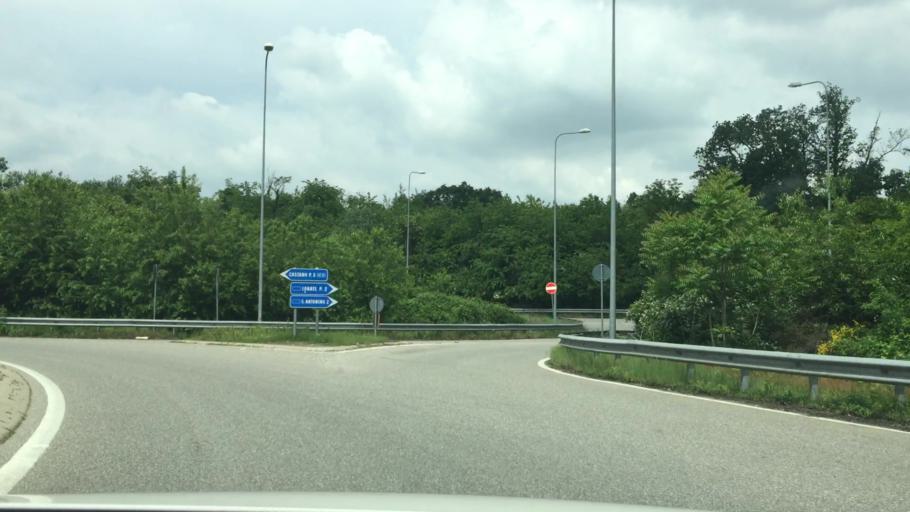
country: IT
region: Lombardy
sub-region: Provincia di Varese
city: Lonate Pozzolo
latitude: 45.5715
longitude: 8.7435
